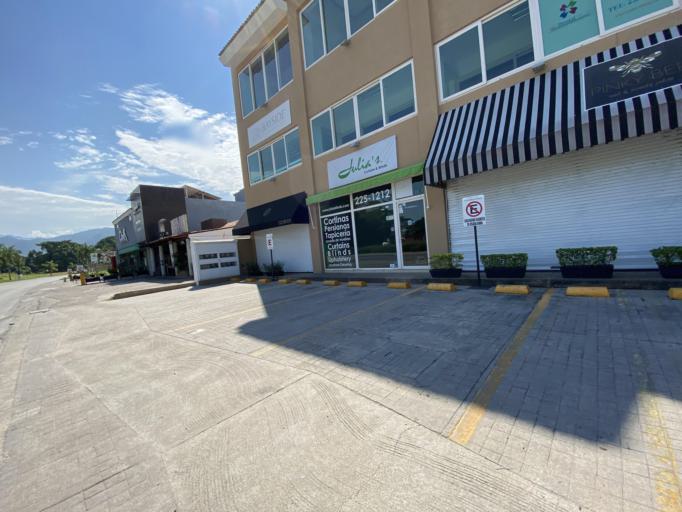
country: MX
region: Jalisco
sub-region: Puerto Vallarta
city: Puerto Vallarta
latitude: 20.6412
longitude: -105.2270
